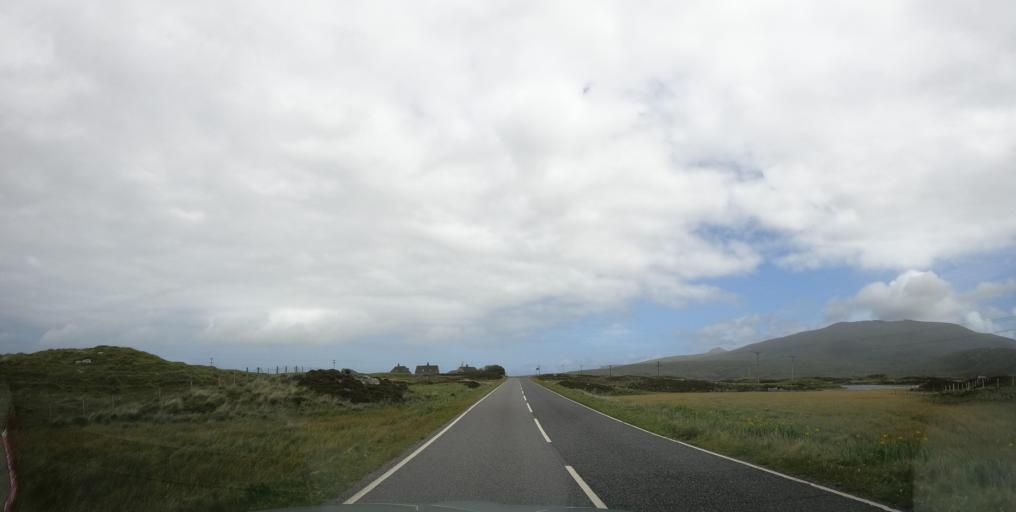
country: GB
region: Scotland
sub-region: Eilean Siar
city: Isle of South Uist
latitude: 57.2475
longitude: -7.3813
